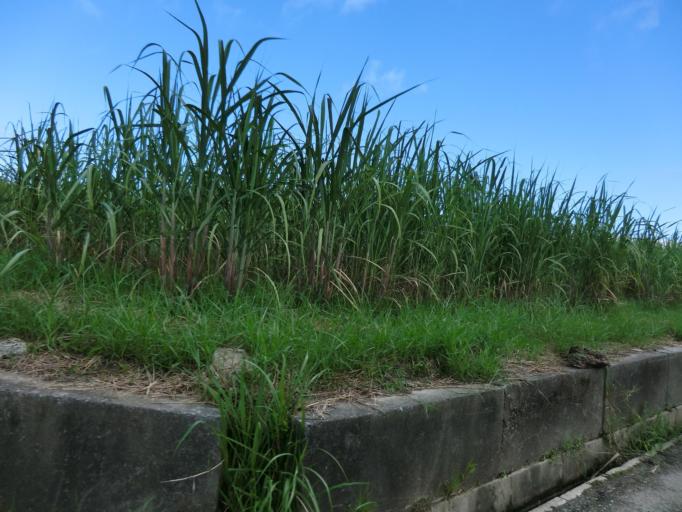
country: JP
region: Okinawa
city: Tomigusuku
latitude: 26.1588
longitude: 127.6670
